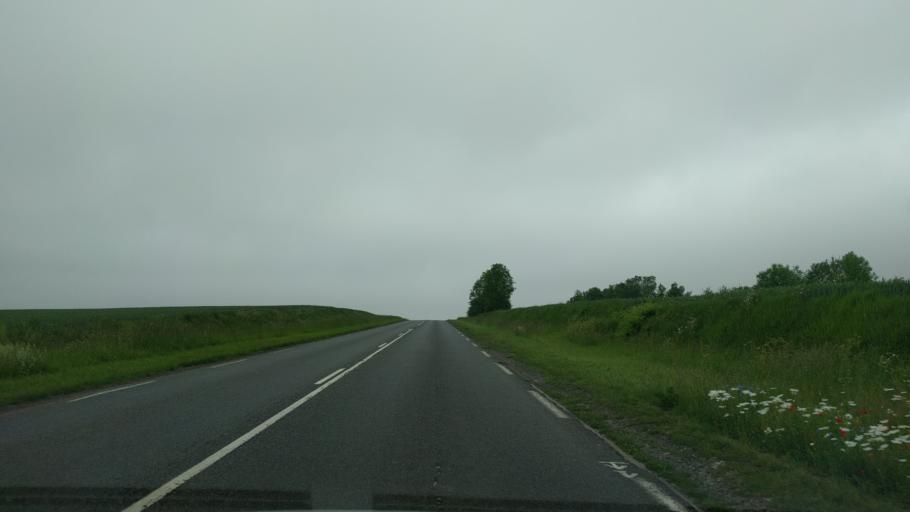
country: FR
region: Picardie
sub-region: Departement de la Somme
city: Peronne
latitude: 49.9634
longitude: 2.9235
